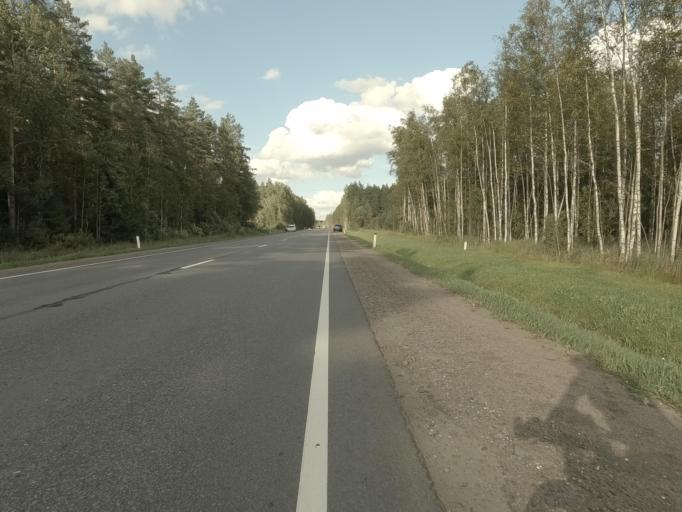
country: RU
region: Leningrad
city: Mga
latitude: 59.7108
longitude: 31.0242
